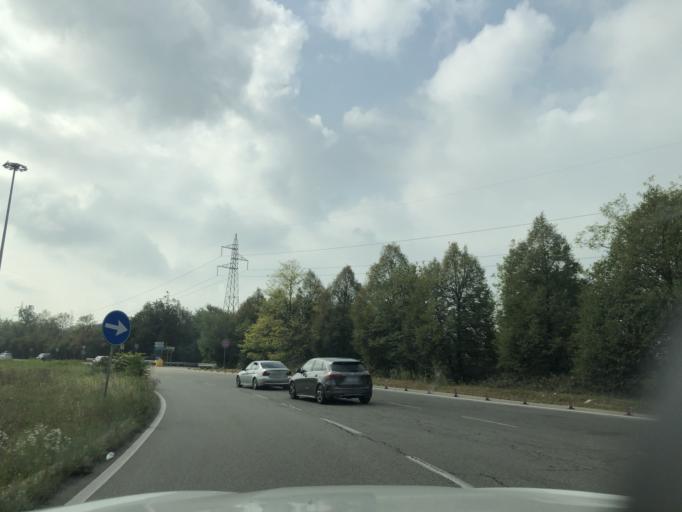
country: IT
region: Lombardy
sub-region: Provincia di Varese
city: Vizzola Ticino
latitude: 45.6272
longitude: 8.7049
